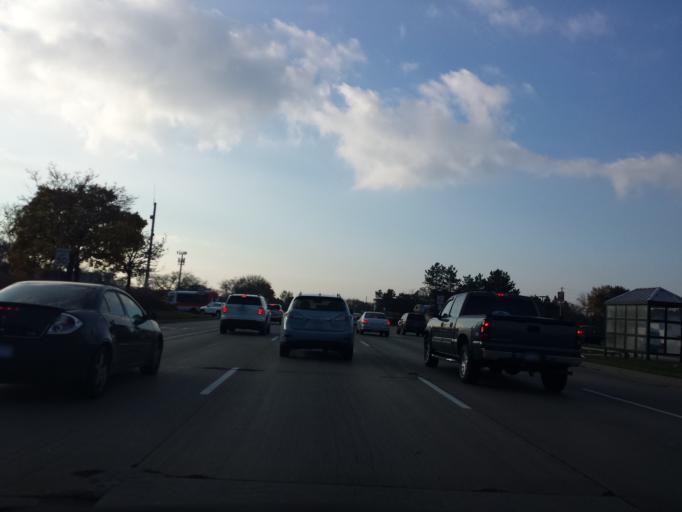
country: US
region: Michigan
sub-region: Oakland County
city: Franklin
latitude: 42.5437
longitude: -83.2852
